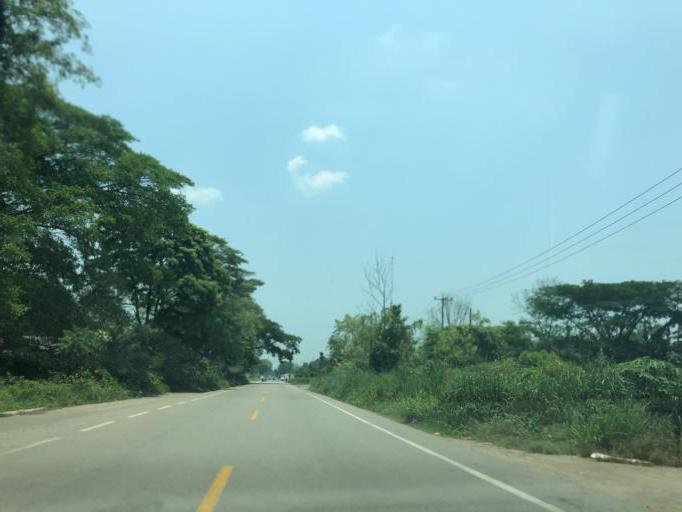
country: MX
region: Tabasco
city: Teapa
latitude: 17.5881
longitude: -92.9668
